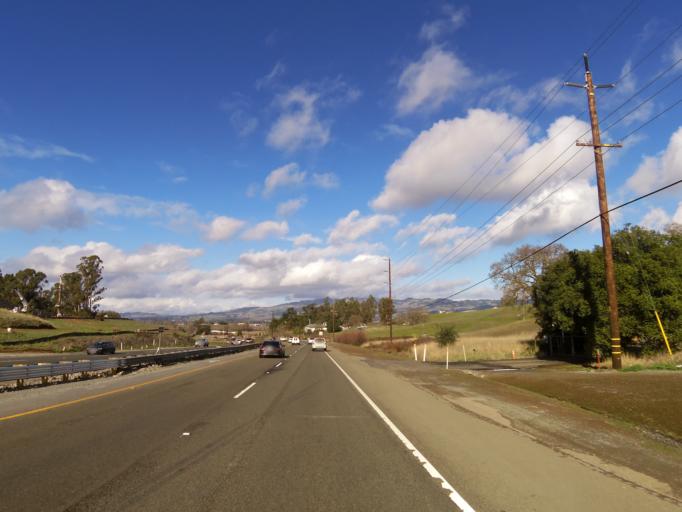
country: US
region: California
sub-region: Sonoma County
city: Petaluma
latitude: 38.2027
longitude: -122.5981
